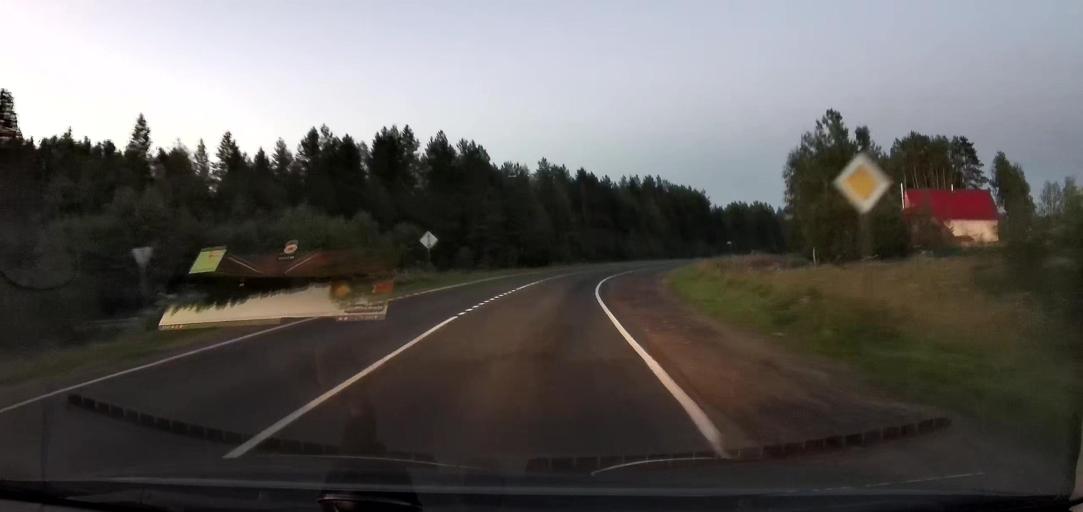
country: RU
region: Arkhangelskaya
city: Uyemskiy
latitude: 64.4146
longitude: 40.9958
